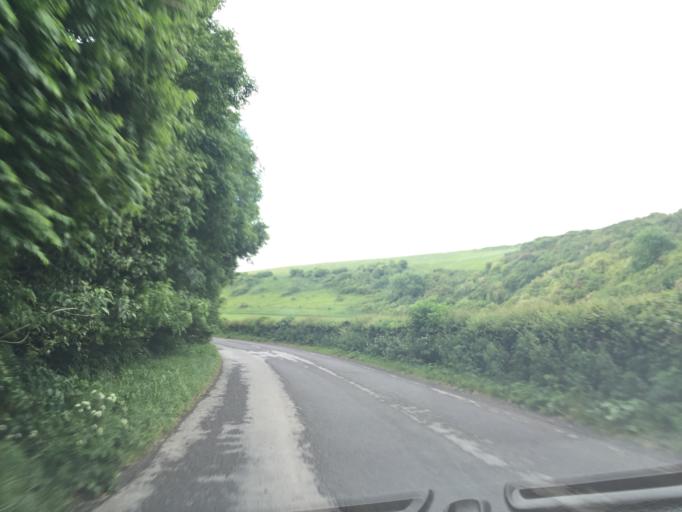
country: GB
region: England
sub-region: Dorset
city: Wool
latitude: 50.6465
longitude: -2.2674
